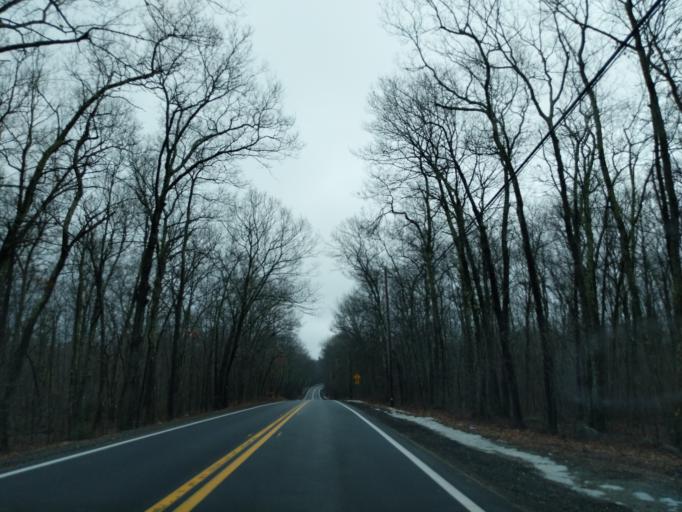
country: US
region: Massachusetts
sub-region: Worcester County
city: Douglas
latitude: 42.0571
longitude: -71.8065
